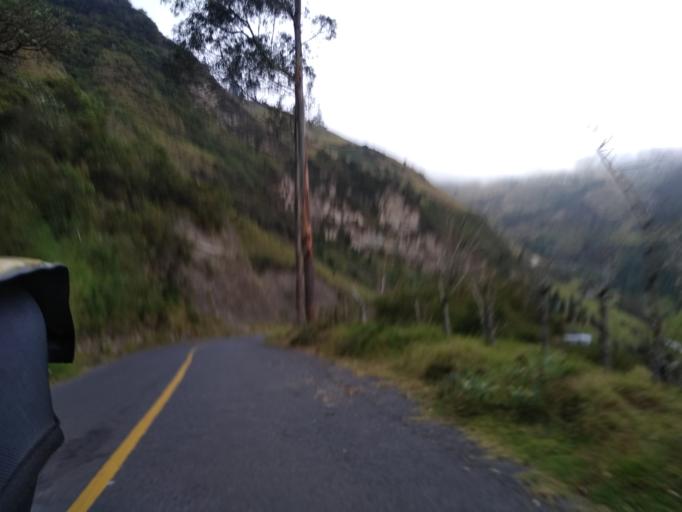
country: EC
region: Cotopaxi
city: Saquisili
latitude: -0.6887
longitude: -78.8657
